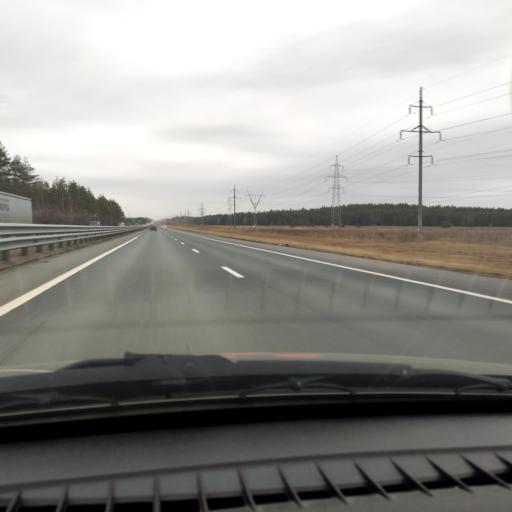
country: RU
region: Samara
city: Povolzhskiy
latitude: 53.5151
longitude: 49.6617
